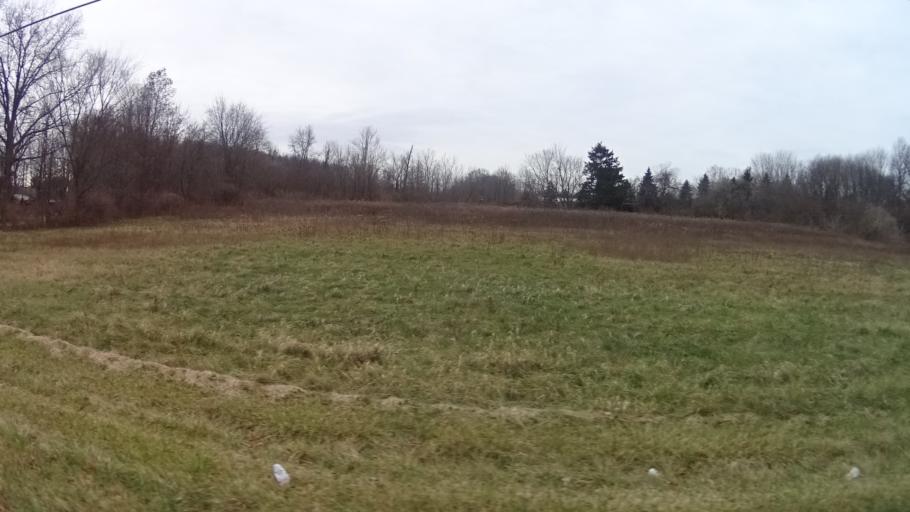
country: US
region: Ohio
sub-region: Lorain County
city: North Ridgeville
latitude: 41.3720
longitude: -81.9899
